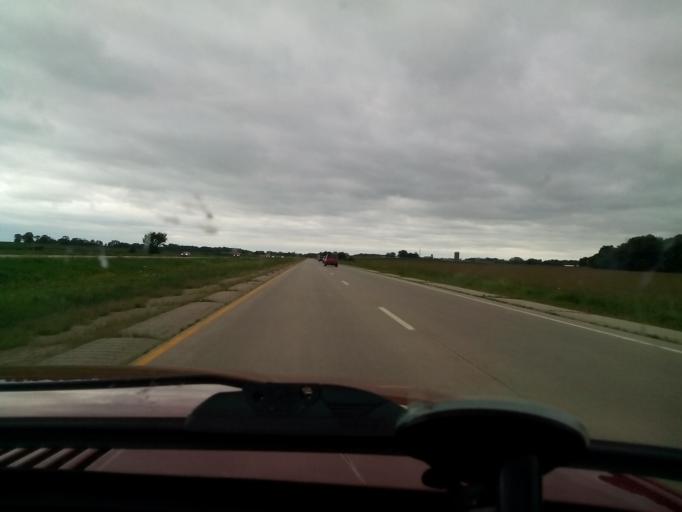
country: US
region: Wisconsin
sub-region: Columbia County
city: Columbus
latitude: 43.2886
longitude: -89.0739
